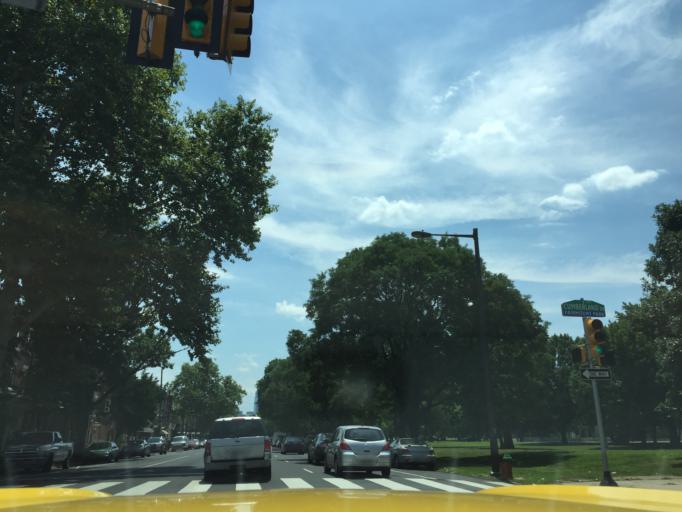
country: US
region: Pennsylvania
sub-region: Montgomery County
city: Bala-Cynwyd
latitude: 39.9951
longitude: -75.1873
